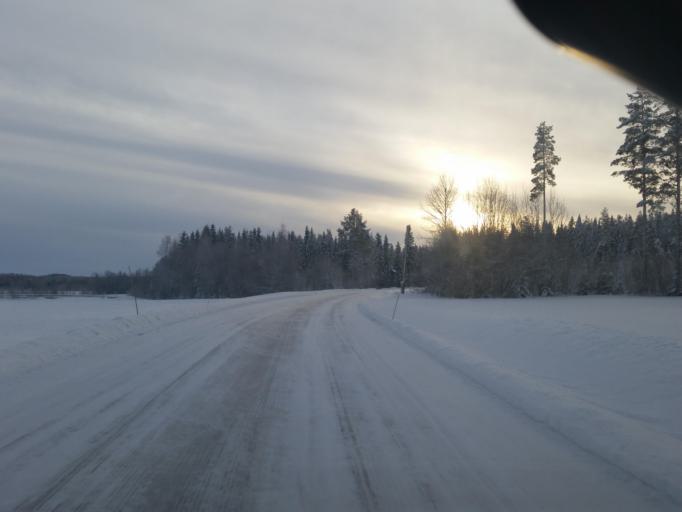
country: SE
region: Norrbotten
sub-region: Pitea Kommun
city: Norrfjarden
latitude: 65.5452
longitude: 21.4911
